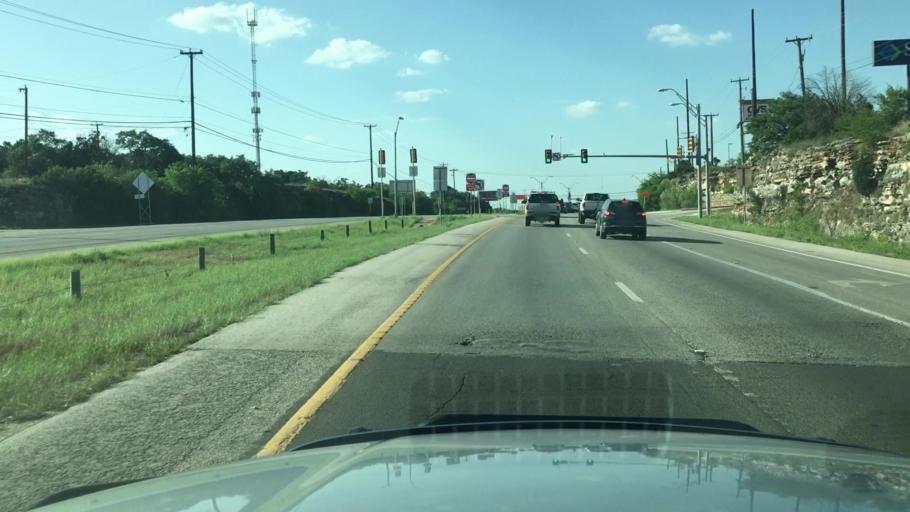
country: US
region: Texas
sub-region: Bexar County
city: Timberwood Park
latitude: 29.6586
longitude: -98.4501
